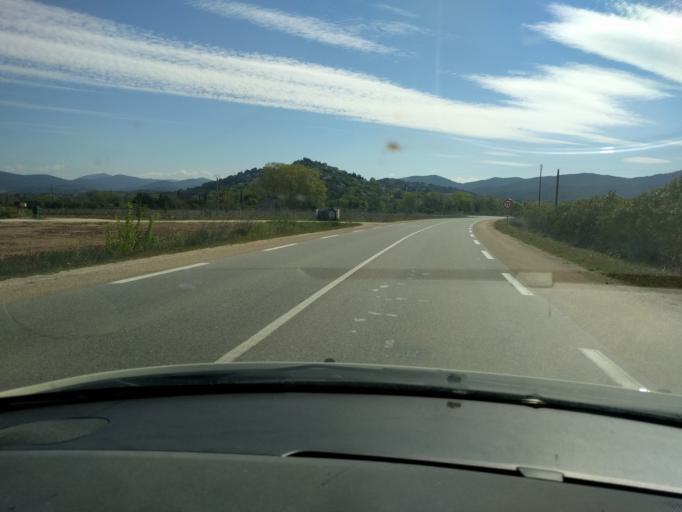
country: FR
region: Provence-Alpes-Cote d'Azur
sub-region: Departement du Var
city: Pierrefeu-du-Var
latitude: 43.2260
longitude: 6.1272
